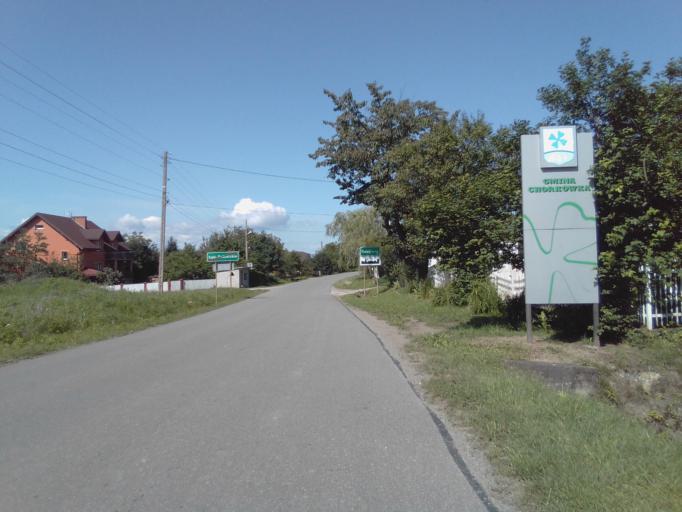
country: PL
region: Subcarpathian Voivodeship
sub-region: Powiat krosnienski
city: Chorkowka
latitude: 49.6052
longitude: 21.6598
